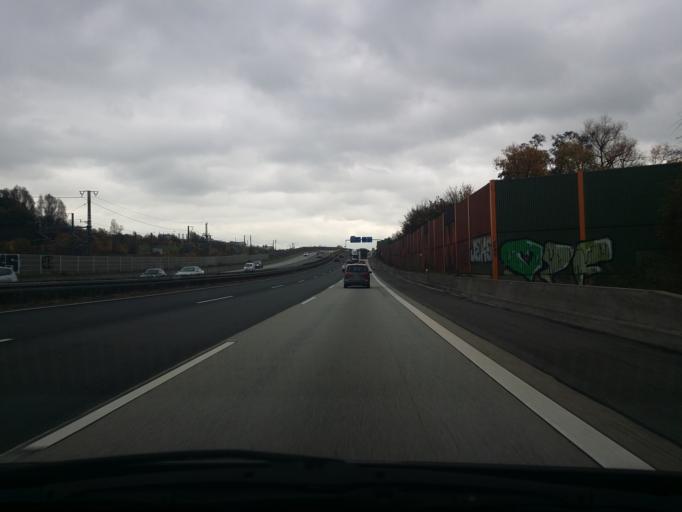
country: DE
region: Hesse
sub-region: Regierungsbezirk Darmstadt
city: Hochheim am Main
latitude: 50.0714
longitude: 8.3730
